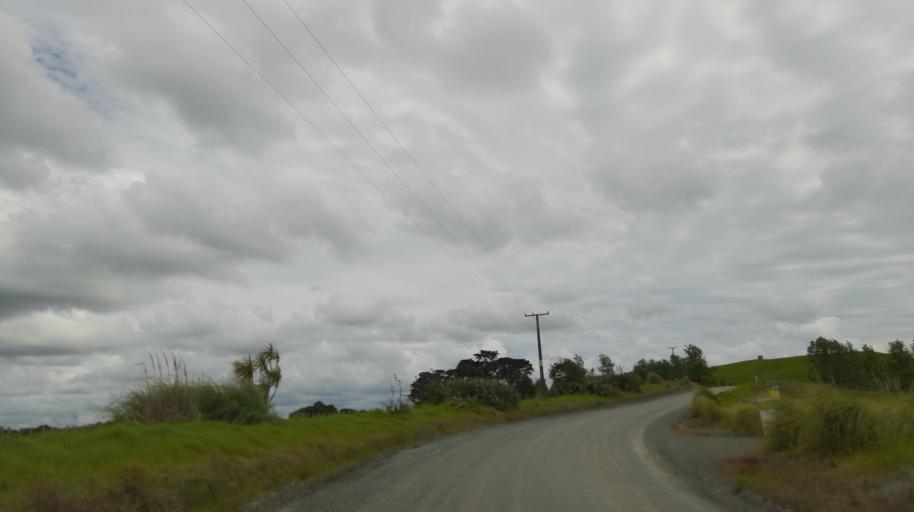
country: NZ
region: Auckland
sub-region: Auckland
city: Wellsford
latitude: -36.2386
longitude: 174.4384
